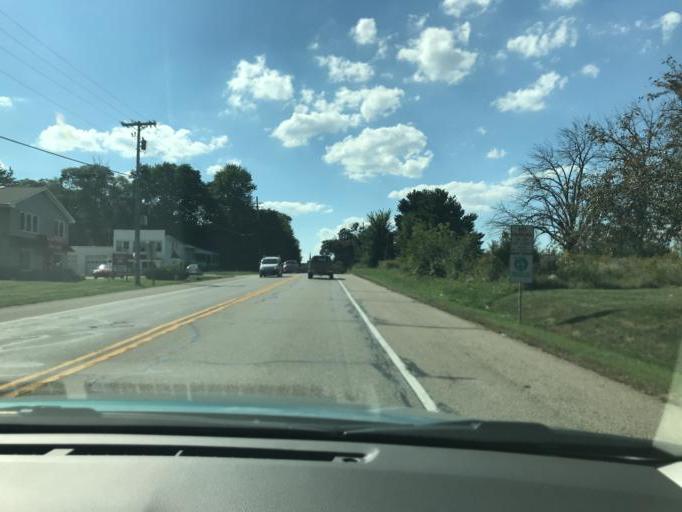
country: US
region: Wisconsin
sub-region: Walworth County
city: Lake Geneva
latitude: 42.5928
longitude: -88.4166
